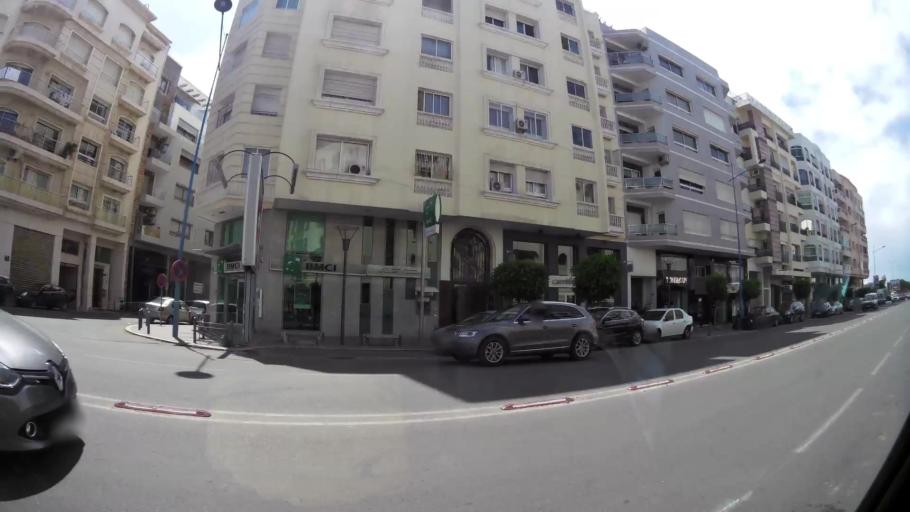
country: MA
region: Grand Casablanca
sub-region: Casablanca
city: Casablanca
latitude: 33.5934
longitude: -7.6436
